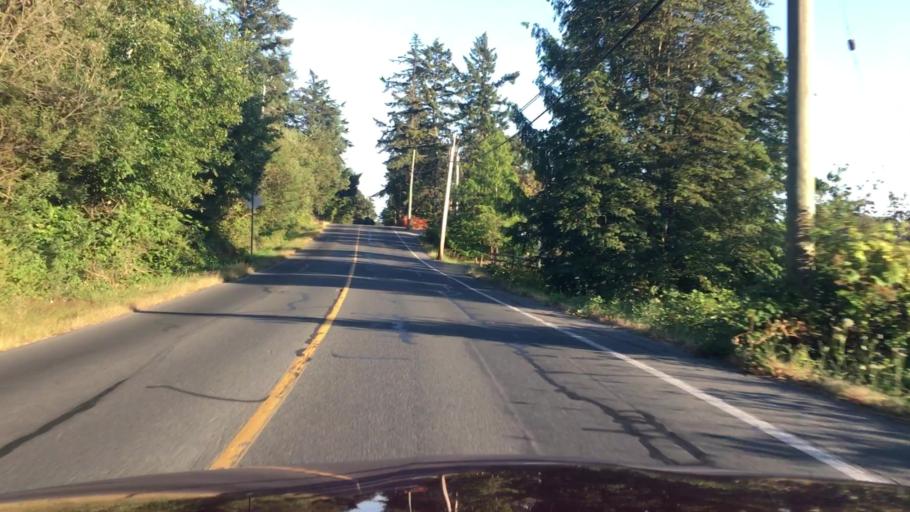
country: CA
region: British Columbia
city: Victoria
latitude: 48.4890
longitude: -123.3562
